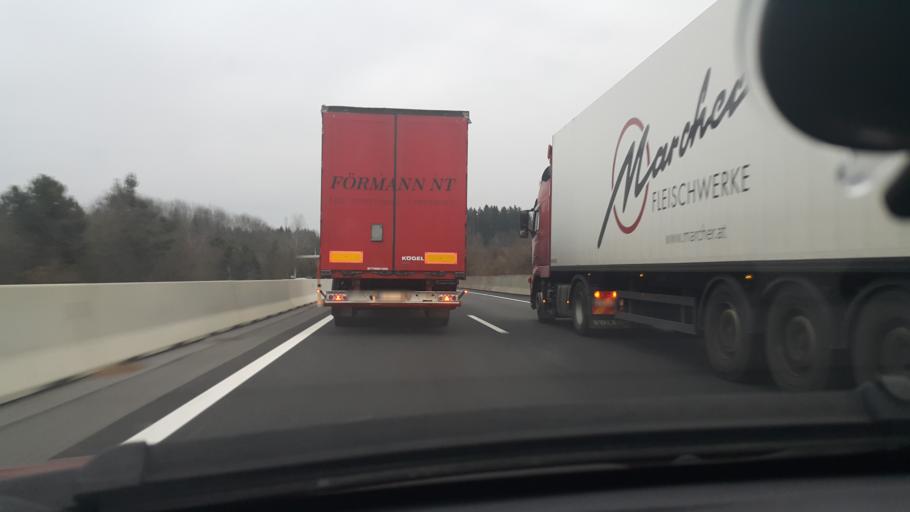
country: AT
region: Carinthia
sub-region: Politischer Bezirk Volkermarkt
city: Voelkermarkt
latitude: 46.6781
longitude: 14.6122
